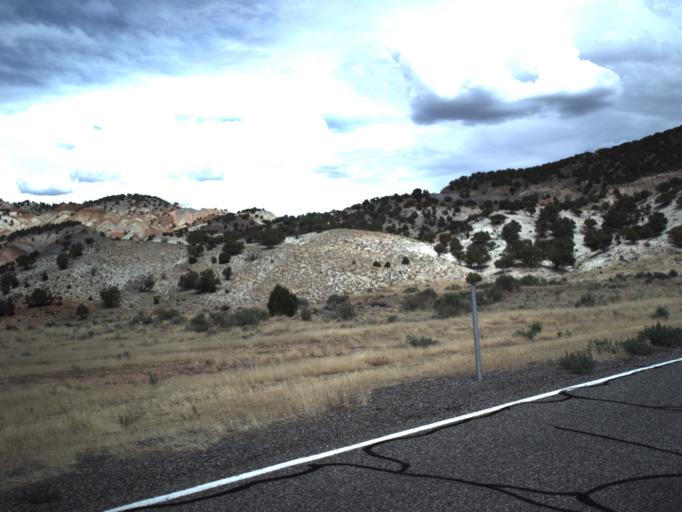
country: US
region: Utah
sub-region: Sevier County
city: Richfield
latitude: 38.7757
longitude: -111.9518
